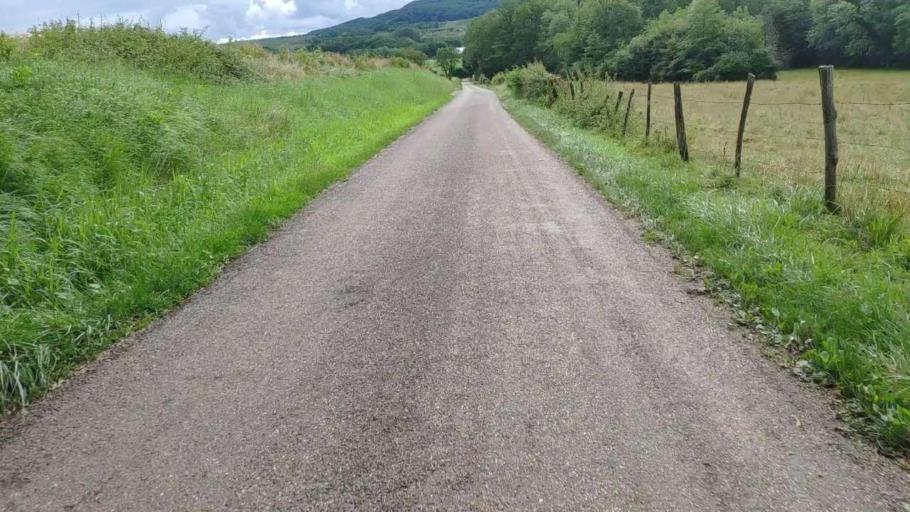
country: FR
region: Franche-Comte
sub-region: Departement du Jura
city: Poligny
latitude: 46.8020
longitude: 5.5943
